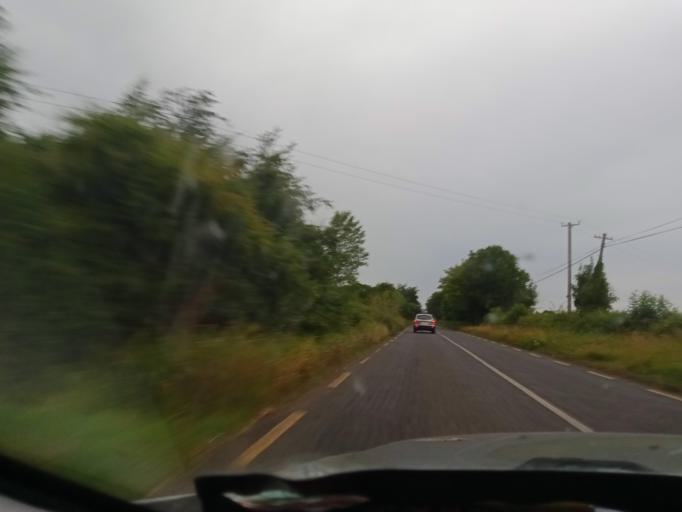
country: IE
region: Leinster
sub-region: Laois
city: Mountmellick
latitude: 53.1207
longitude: -7.3660
